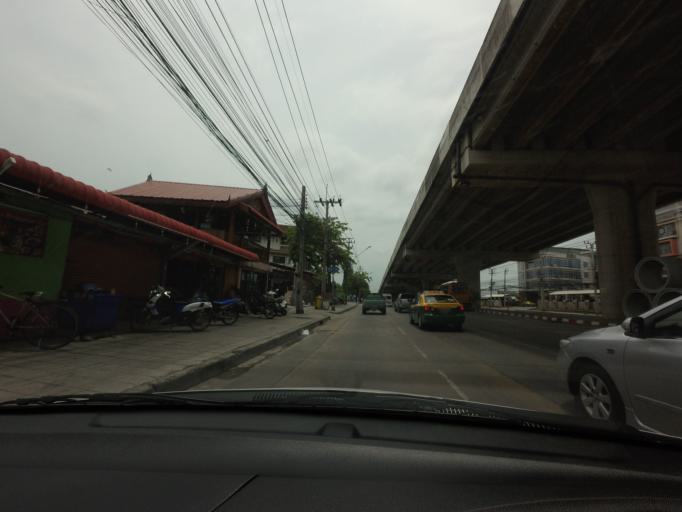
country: TH
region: Bangkok
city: Min Buri
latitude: 13.8196
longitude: 100.7400
